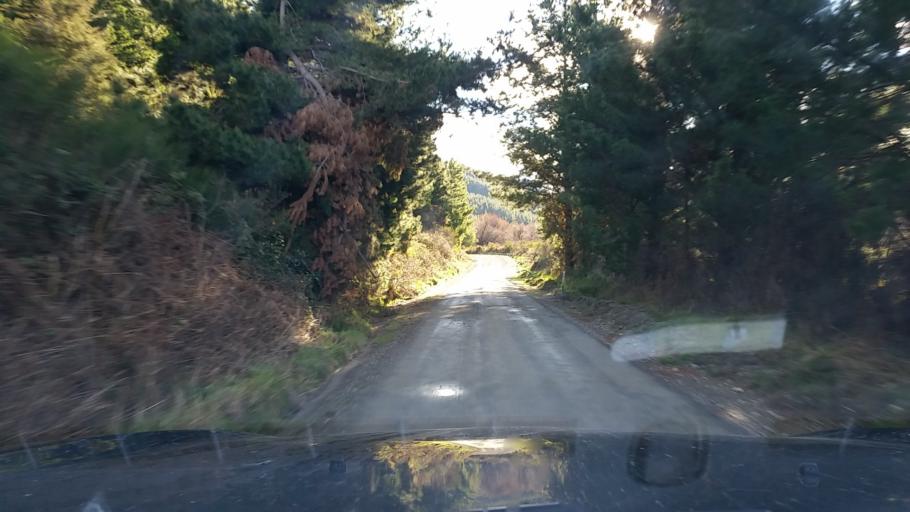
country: NZ
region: Nelson
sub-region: Nelson City
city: Nelson
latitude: -41.5639
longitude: 173.4382
